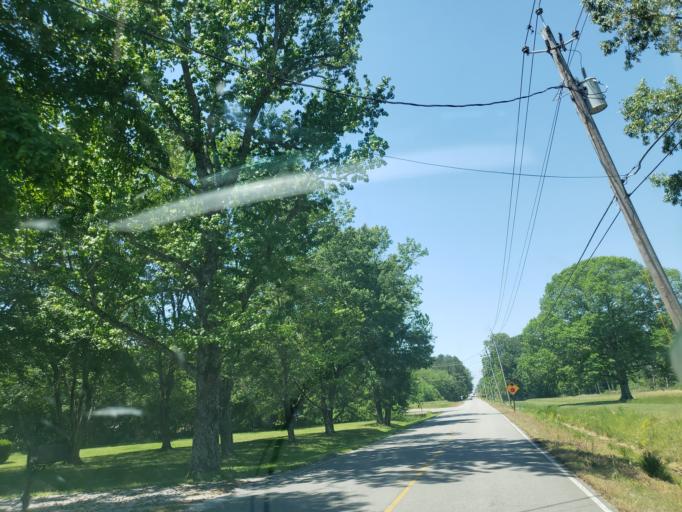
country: US
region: Alabama
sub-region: Madison County
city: Harvest
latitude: 34.9625
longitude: -86.7102
